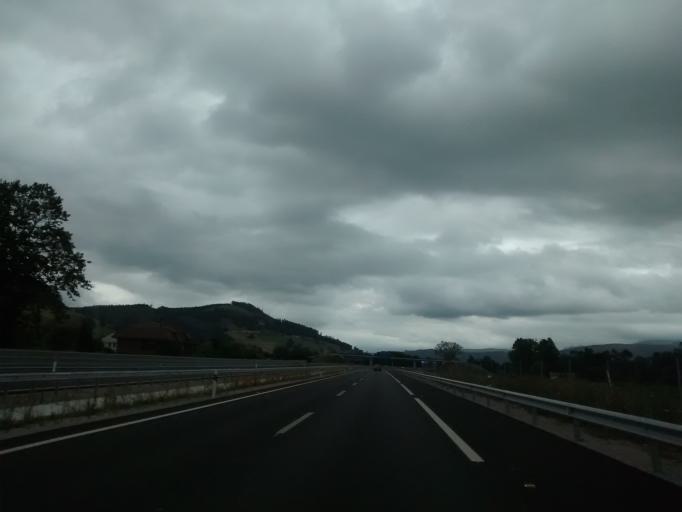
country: ES
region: Cantabria
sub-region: Provincia de Cantabria
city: Villafufre
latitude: 43.3134
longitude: -3.9032
